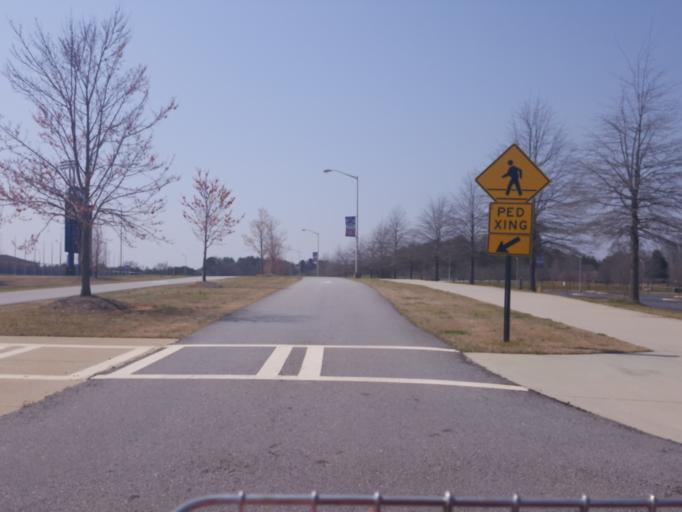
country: US
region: Georgia
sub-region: Carroll County
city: Carrollton
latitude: 33.5814
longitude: -85.1193
